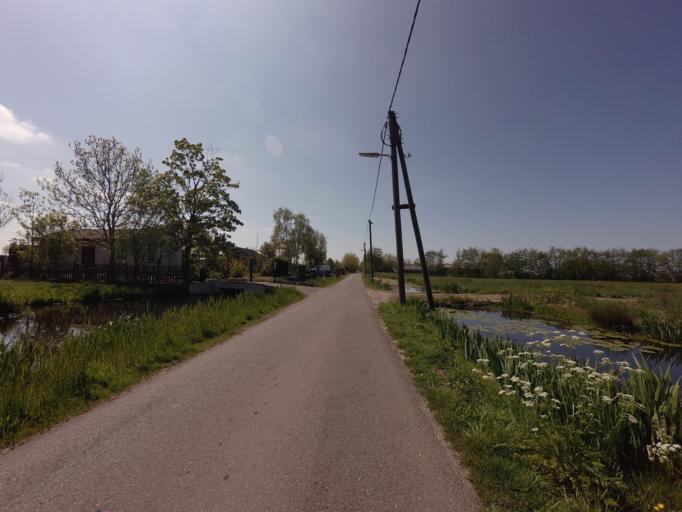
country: NL
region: South Holland
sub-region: Gemeente Gouda
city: Gouda
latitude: 51.9726
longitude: 4.7050
